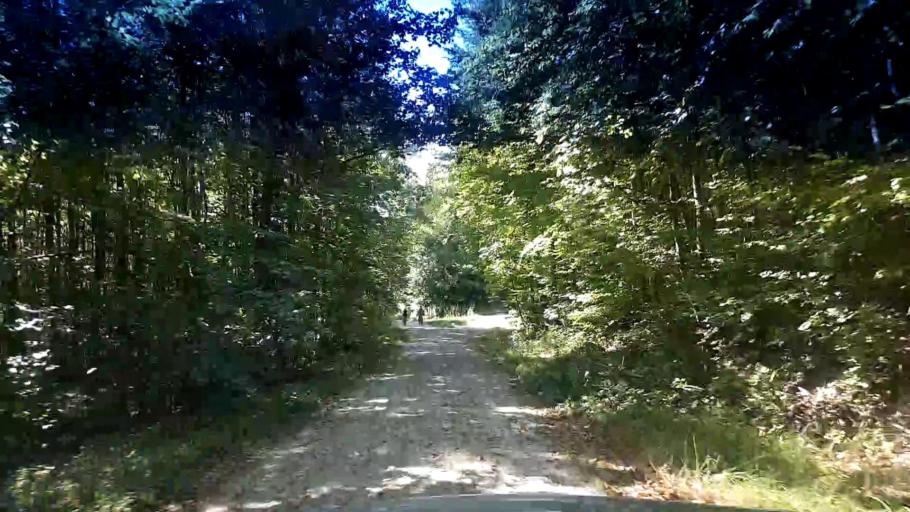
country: DE
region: Bavaria
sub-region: Upper Franconia
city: Litzendorf
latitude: 49.8828
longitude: 11.0712
